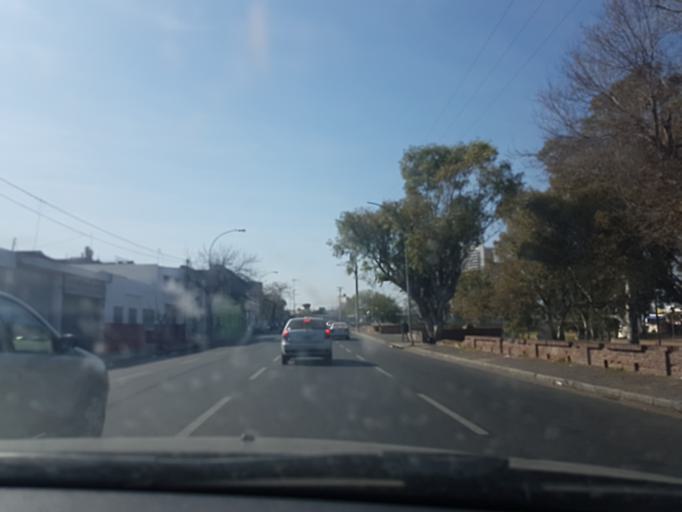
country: AR
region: Cordoba
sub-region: Departamento de Capital
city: Cordoba
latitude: -31.4057
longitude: -64.1788
